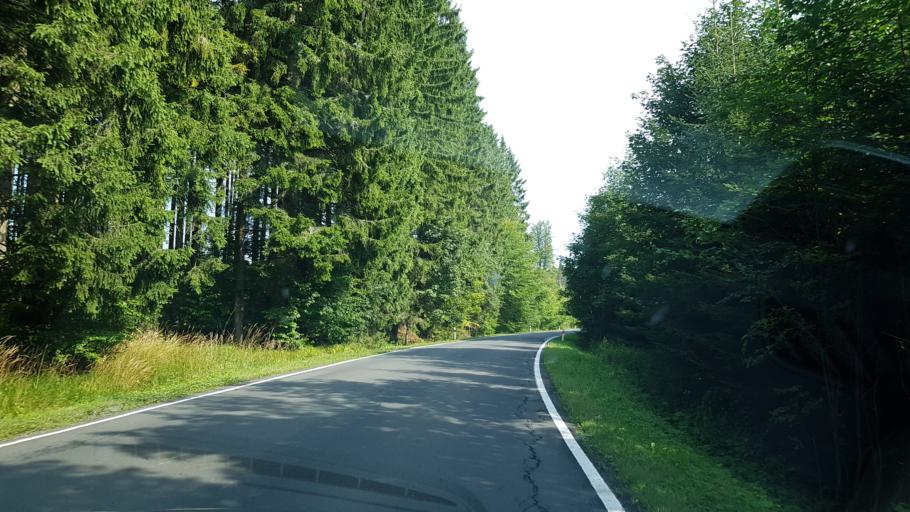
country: CZ
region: Olomoucky
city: Pisecna
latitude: 50.2225
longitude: 17.2730
